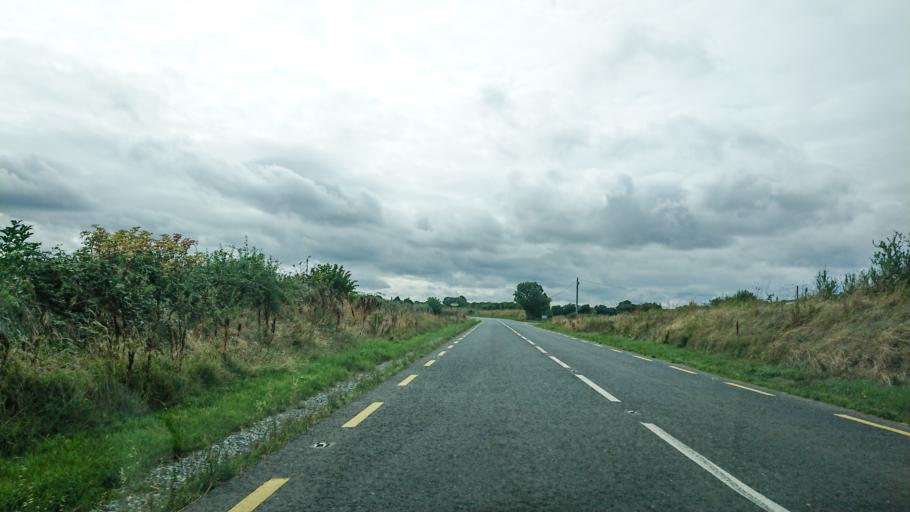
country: IE
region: Munster
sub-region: County Cork
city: Mallow
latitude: 52.1551
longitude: -8.5163
